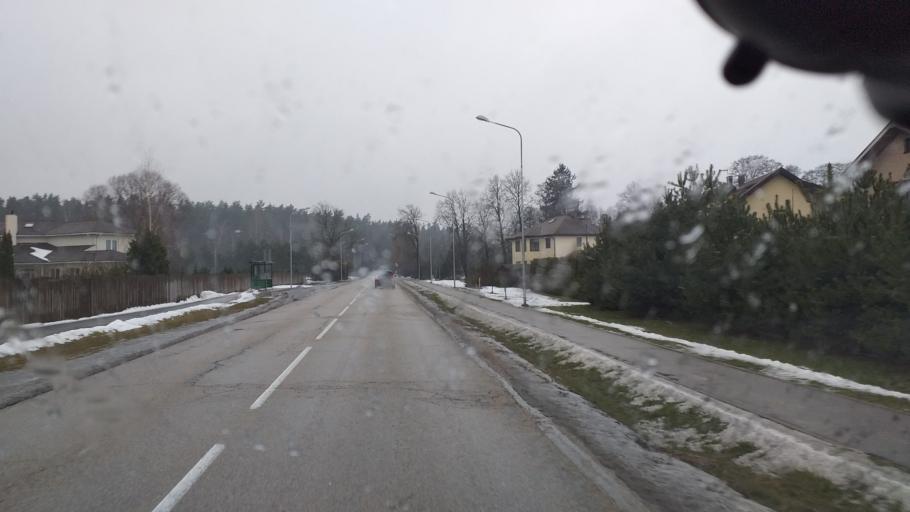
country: LV
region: Riga
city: Daugavgriva
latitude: 56.9848
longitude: 24.0020
